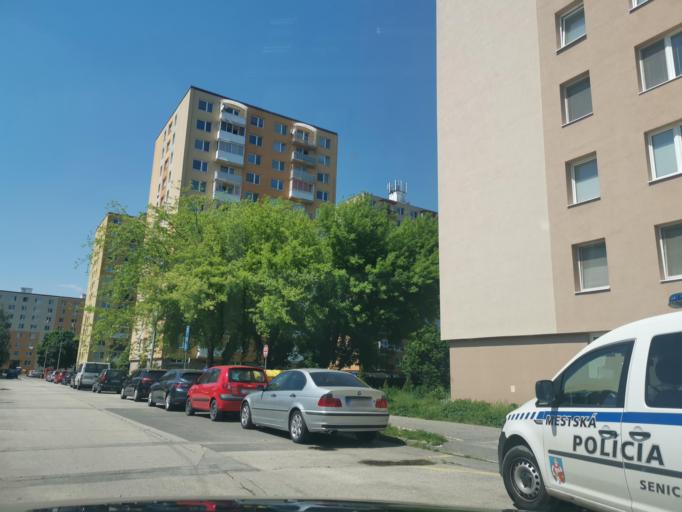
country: SK
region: Trnavsky
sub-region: Okres Senica
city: Senica
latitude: 48.6860
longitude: 17.3757
